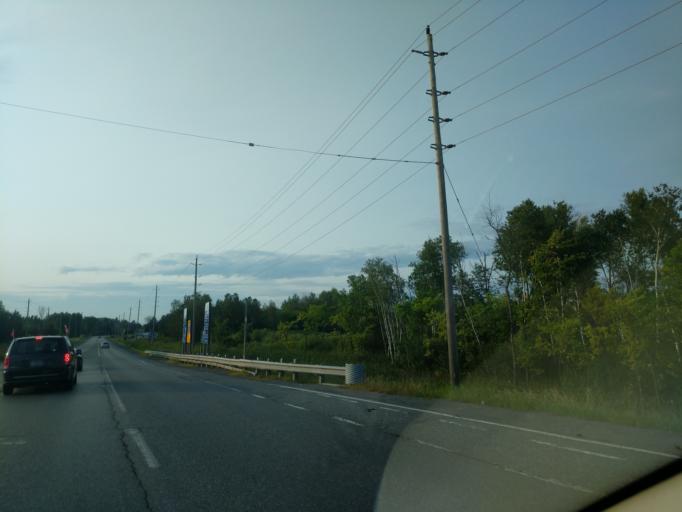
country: CA
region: Ontario
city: Bells Corners
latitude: 45.3152
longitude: -75.8008
